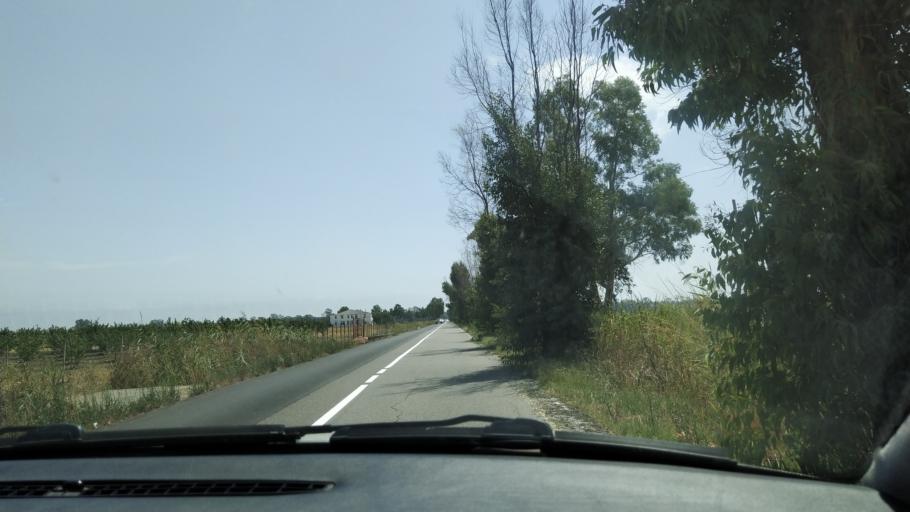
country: IT
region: Basilicate
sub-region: Provincia di Matera
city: Marconia
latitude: 40.3313
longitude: 16.7810
